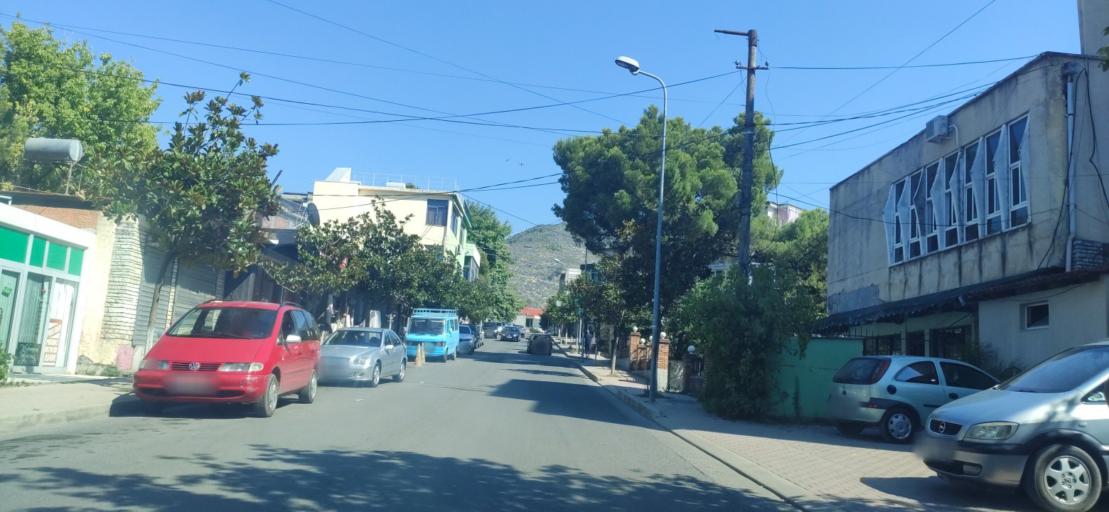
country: AL
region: Lezhe
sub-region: Rrethi i Kurbinit
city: Lac
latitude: 41.6387
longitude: 19.7127
